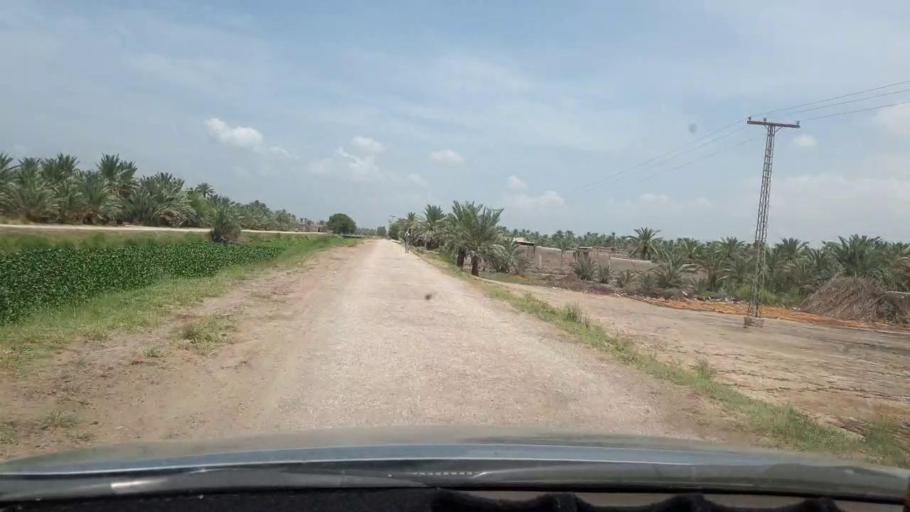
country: PK
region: Sindh
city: Khairpur
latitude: 27.4475
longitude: 68.7854
